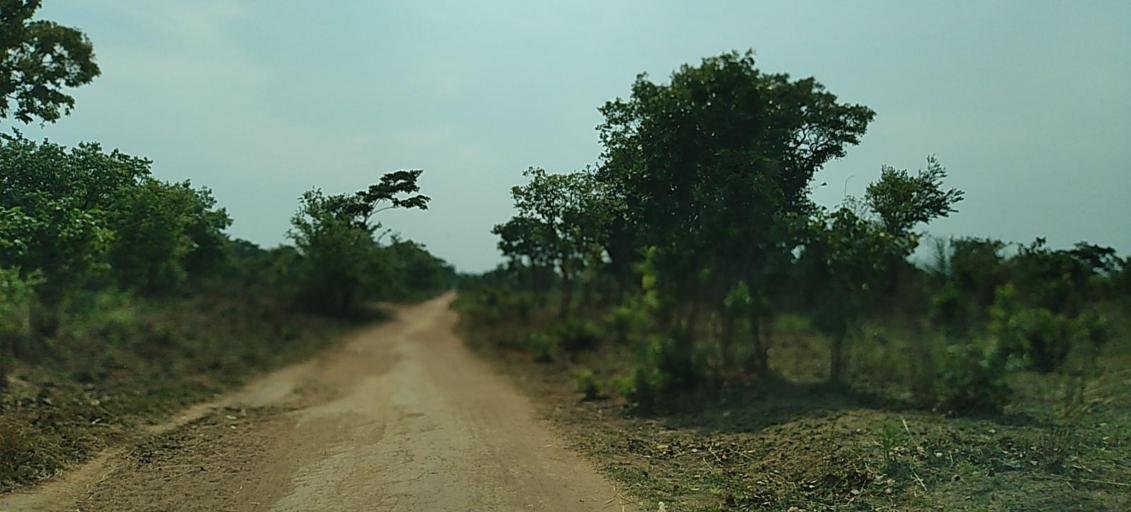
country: ZM
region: Copperbelt
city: Ndola
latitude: -13.2099
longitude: 28.7397
